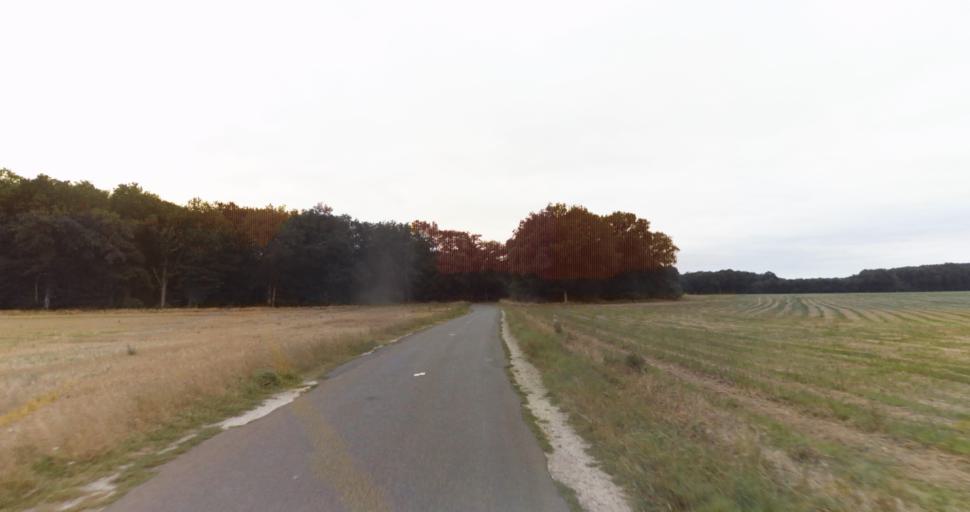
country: FR
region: Haute-Normandie
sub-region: Departement de l'Eure
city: Marcilly-sur-Eure
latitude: 48.8379
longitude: 1.3105
